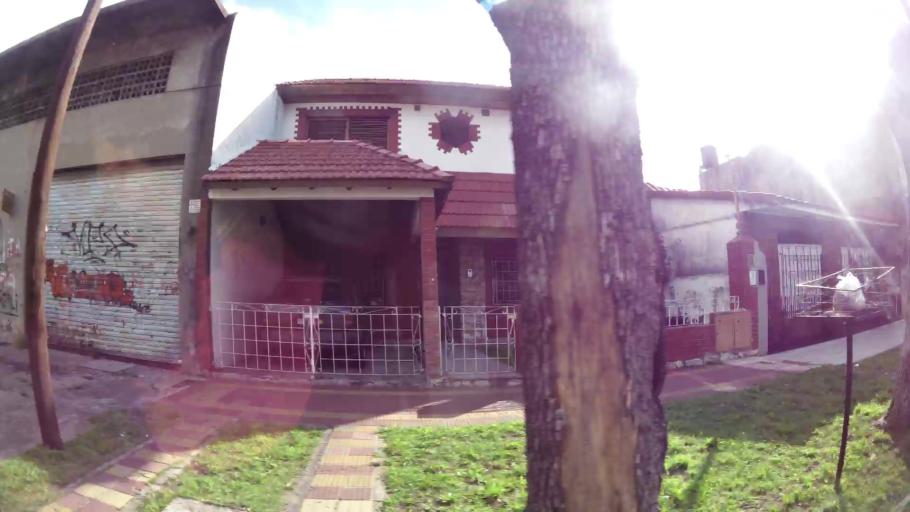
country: AR
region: Buenos Aires
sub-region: Partido de Lanus
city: Lanus
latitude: -34.6932
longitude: -58.3711
